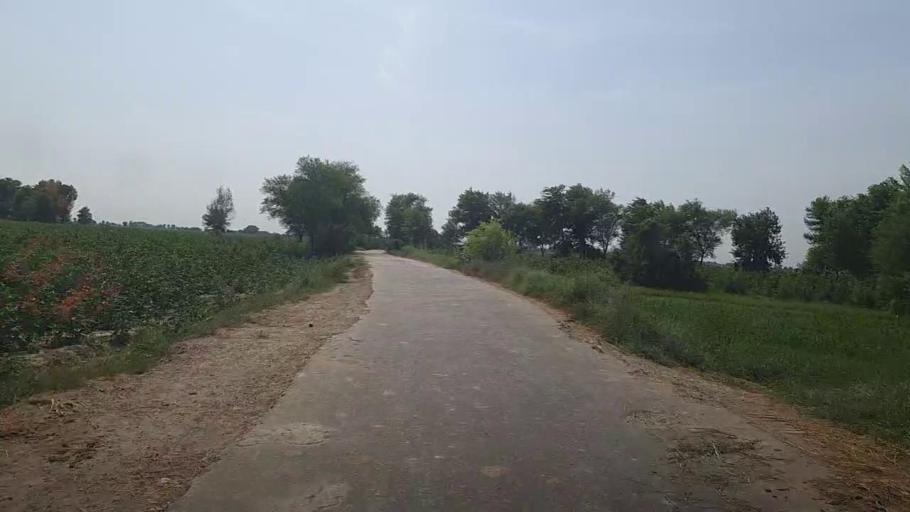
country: PK
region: Sindh
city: Ubauro
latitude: 28.1344
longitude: 69.8328
